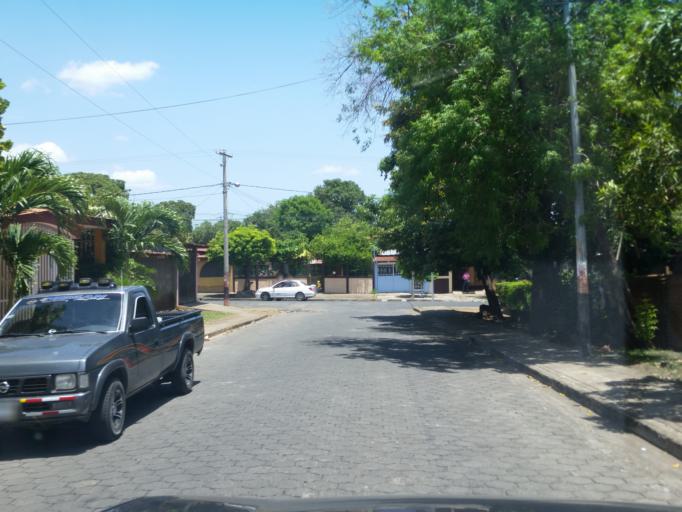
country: NI
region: Managua
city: Managua
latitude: 12.1202
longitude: -86.2402
